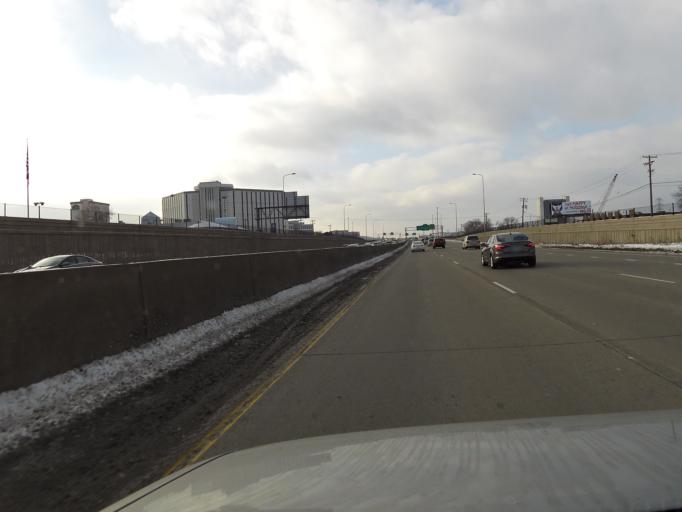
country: US
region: Minnesota
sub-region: Hennepin County
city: Edina
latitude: 44.8584
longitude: -93.3415
